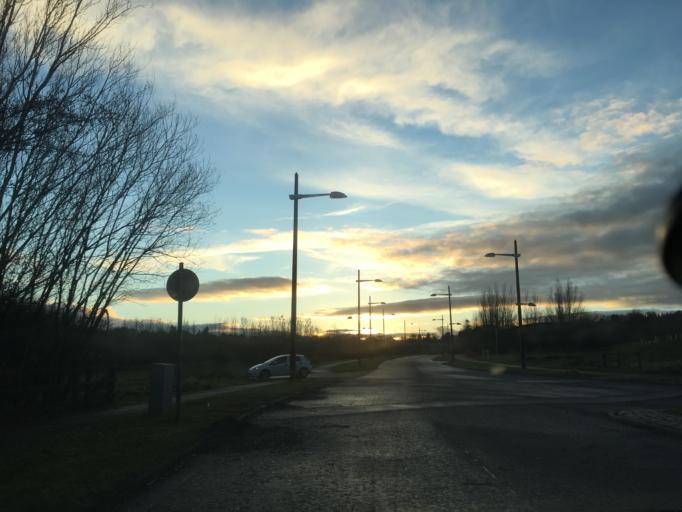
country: GB
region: Scotland
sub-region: Midlothian
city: Loanhead
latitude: 55.8616
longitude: -3.1874
